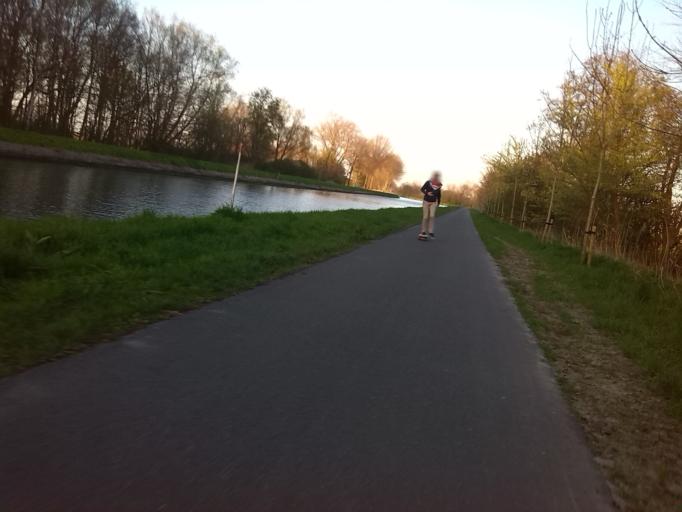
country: BE
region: Flanders
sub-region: Provincie West-Vlaanderen
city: Jabbeke
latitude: 51.2090
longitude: 3.1306
